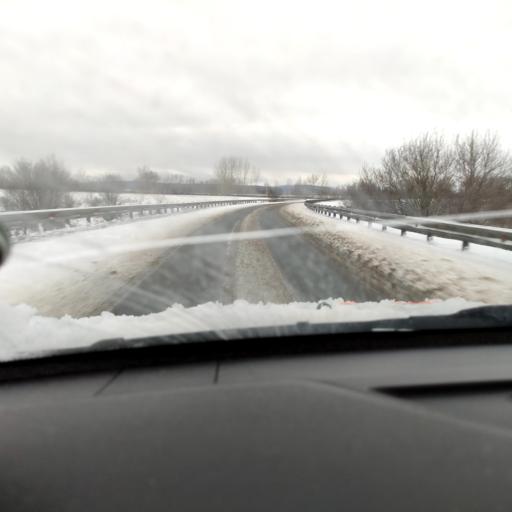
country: RU
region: Samara
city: Novosemeykino
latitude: 53.4172
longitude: 50.3430
